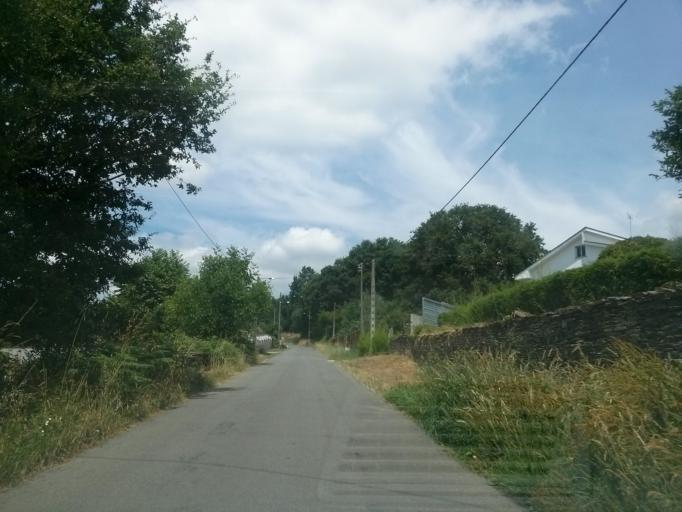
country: ES
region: Galicia
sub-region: Provincia de Lugo
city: Lugo
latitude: 43.0365
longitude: -7.5937
